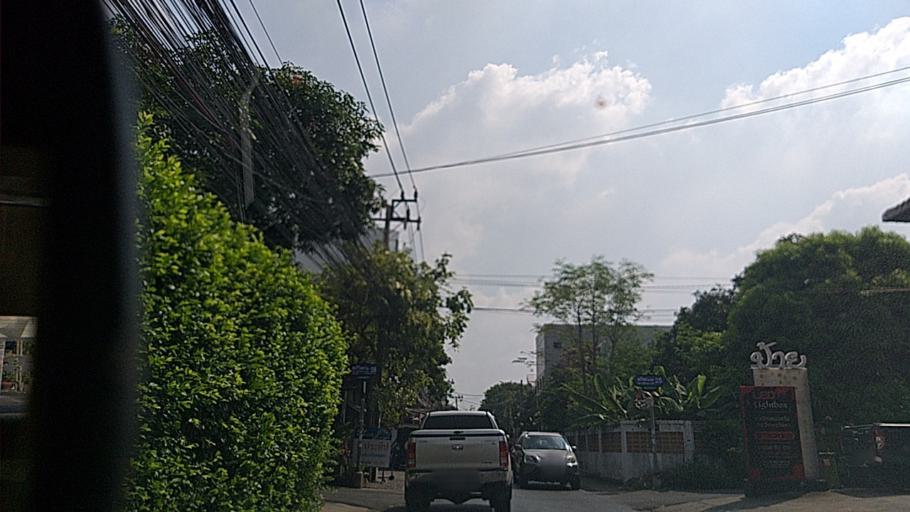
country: TH
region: Bangkok
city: Lat Phrao
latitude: 13.8210
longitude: 100.5981
